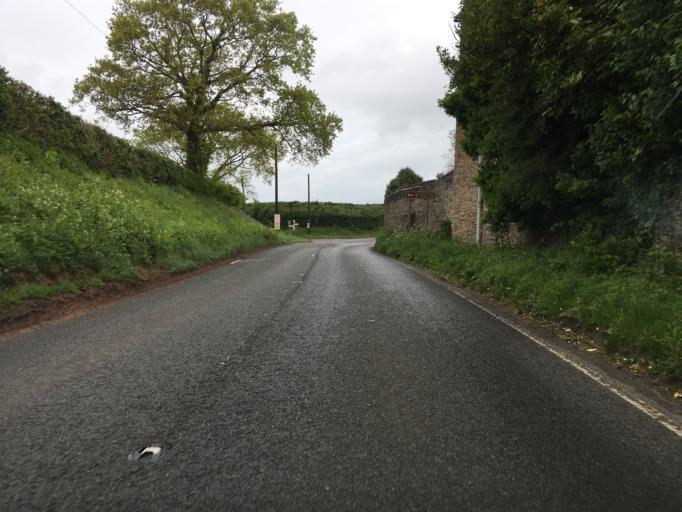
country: GB
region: England
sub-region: Bath and North East Somerset
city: Stanton Drew
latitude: 51.3443
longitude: -2.5773
